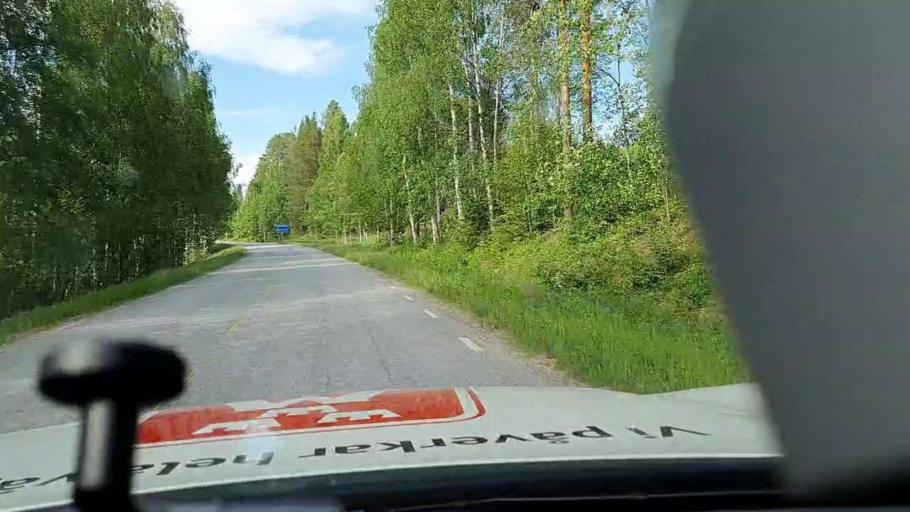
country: SE
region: Norrbotten
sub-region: Gallivare Kommun
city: Gaellivare
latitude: 66.4542
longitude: 20.6570
